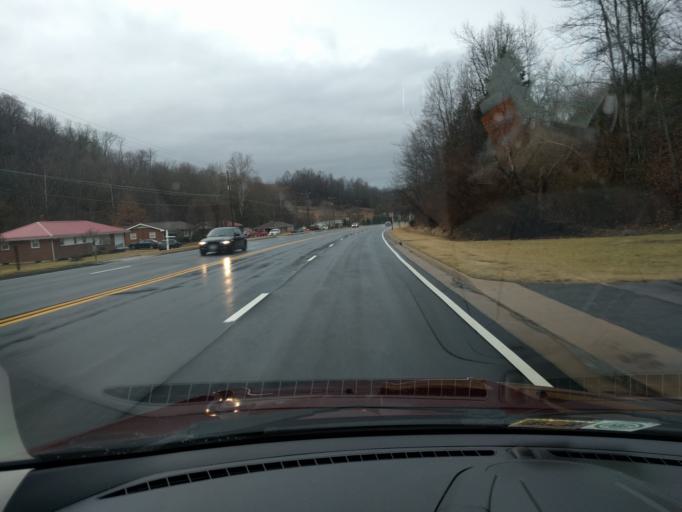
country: US
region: Virginia
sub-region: Giles County
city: Pembroke
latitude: 37.3193
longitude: -80.6192
